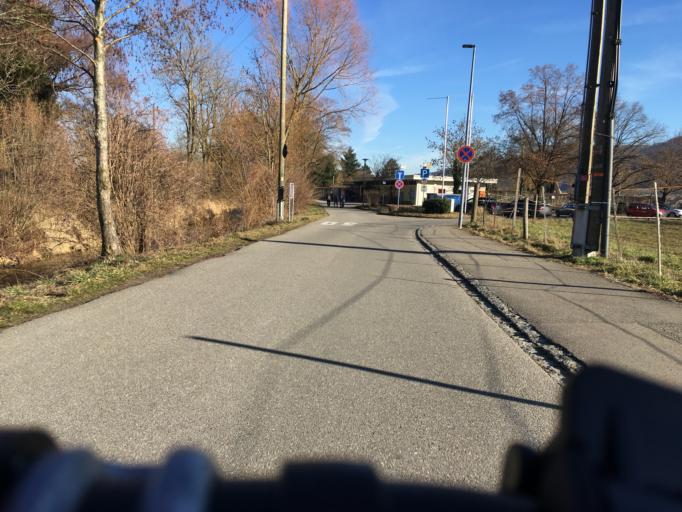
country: DE
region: Baden-Wuerttemberg
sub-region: Freiburg Region
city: Rielasingen-Worblingen
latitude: 47.7215
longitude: 8.8624
